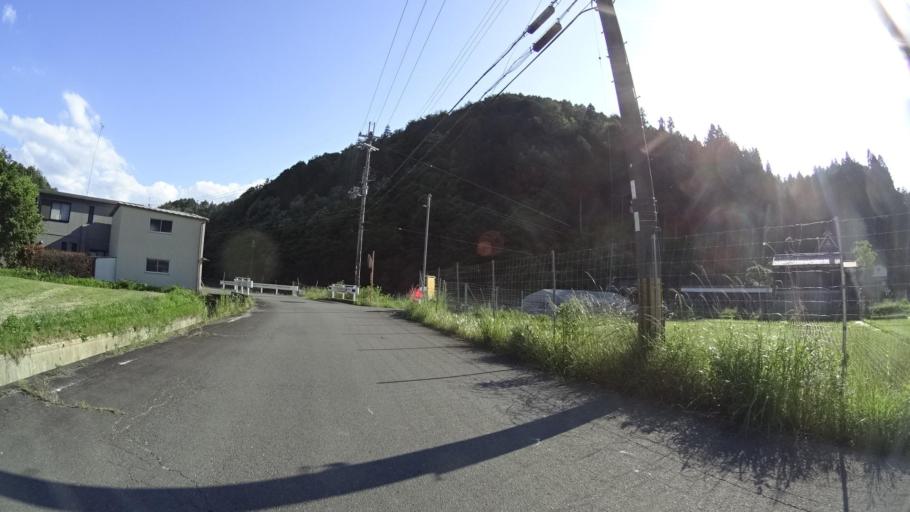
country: JP
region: Kyoto
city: Kameoka
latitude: 34.9778
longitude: 135.5606
